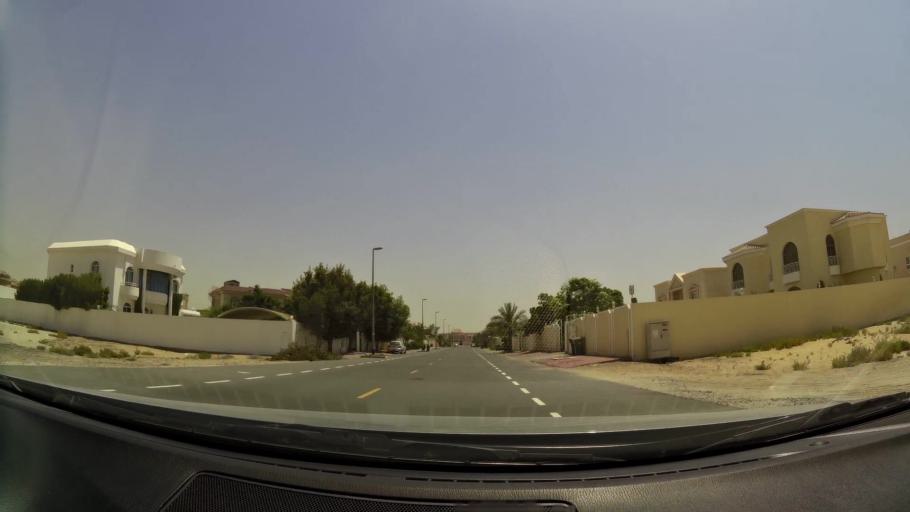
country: AE
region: Dubai
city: Dubai
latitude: 25.0987
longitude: 55.2120
